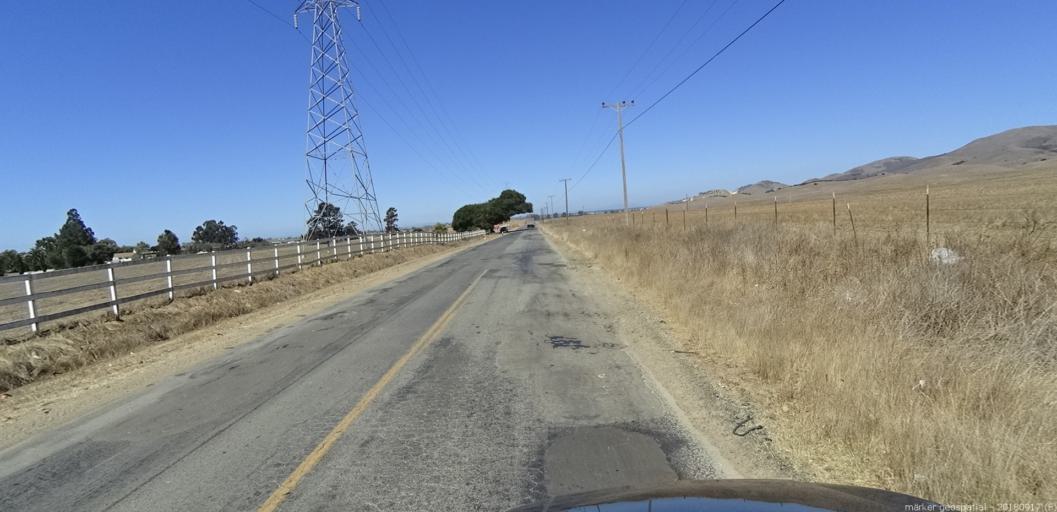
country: US
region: California
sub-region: Monterey County
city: Salinas
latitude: 36.7037
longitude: -121.5788
